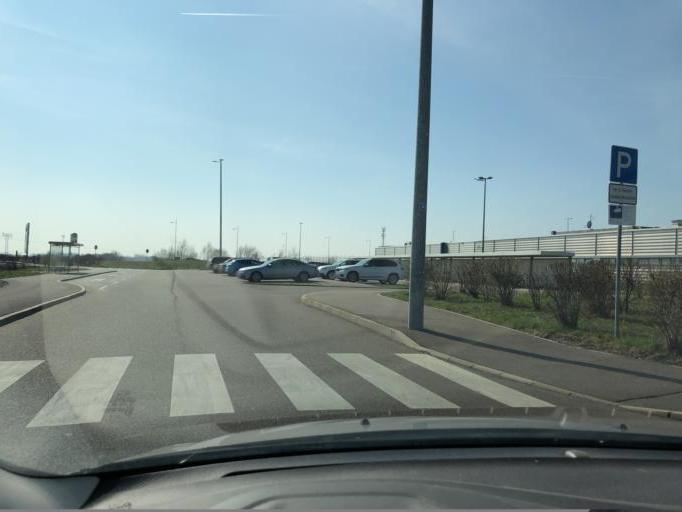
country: DE
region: Saxony
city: Taucha
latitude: 51.4021
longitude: 12.4527
